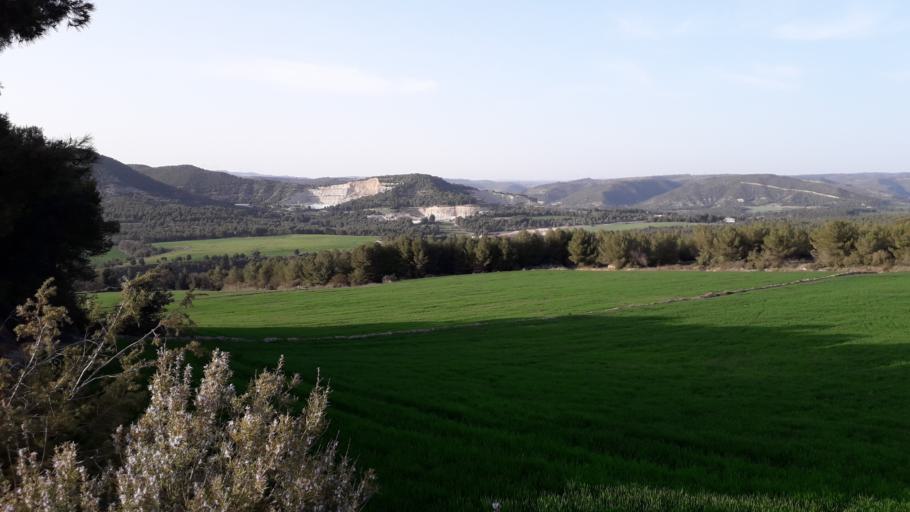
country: ES
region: Catalonia
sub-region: Provincia de Barcelona
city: Jorba
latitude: 41.5916
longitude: 1.5203
